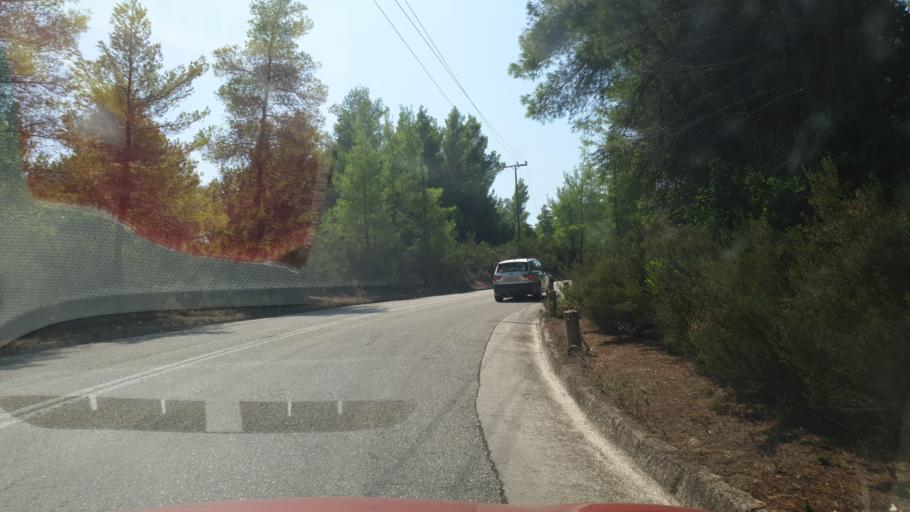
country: GR
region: Central Macedonia
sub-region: Nomos Chalkidikis
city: Sarti
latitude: 40.1425
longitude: 23.9224
